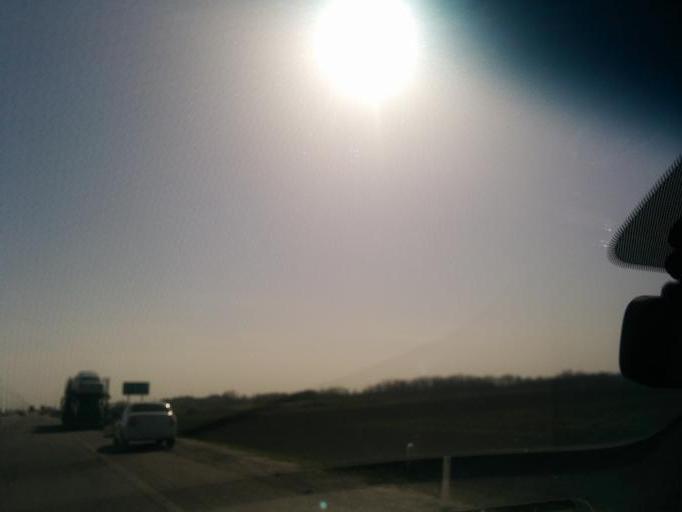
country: RU
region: Rostov
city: Mayskiy
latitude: 47.7101
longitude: 40.0998
